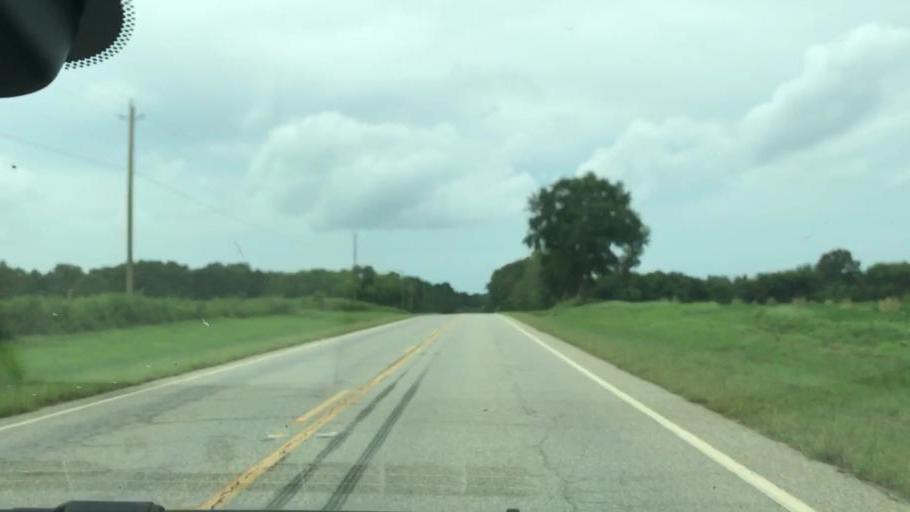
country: US
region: Georgia
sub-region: Clay County
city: Fort Gaines
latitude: 31.7194
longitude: -85.0433
